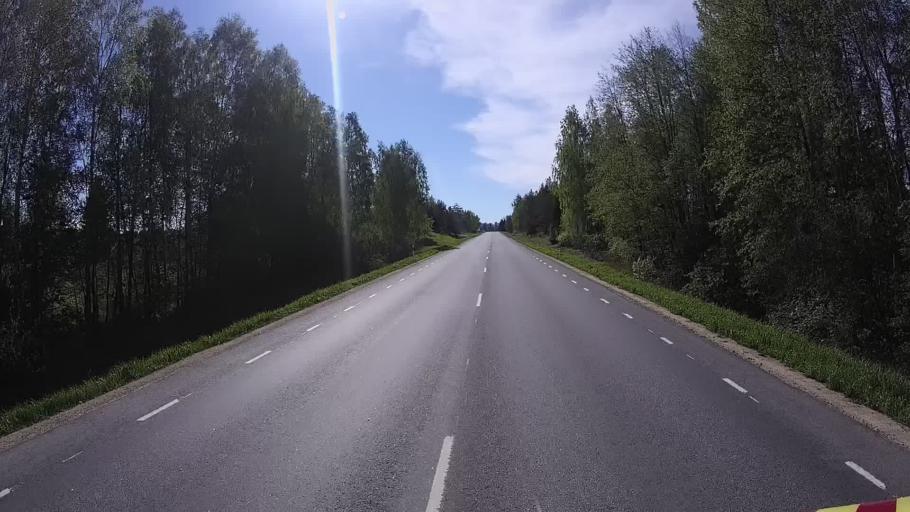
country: EE
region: Tartu
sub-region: UElenurme vald
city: Ulenurme
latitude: 58.3455
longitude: 26.9434
